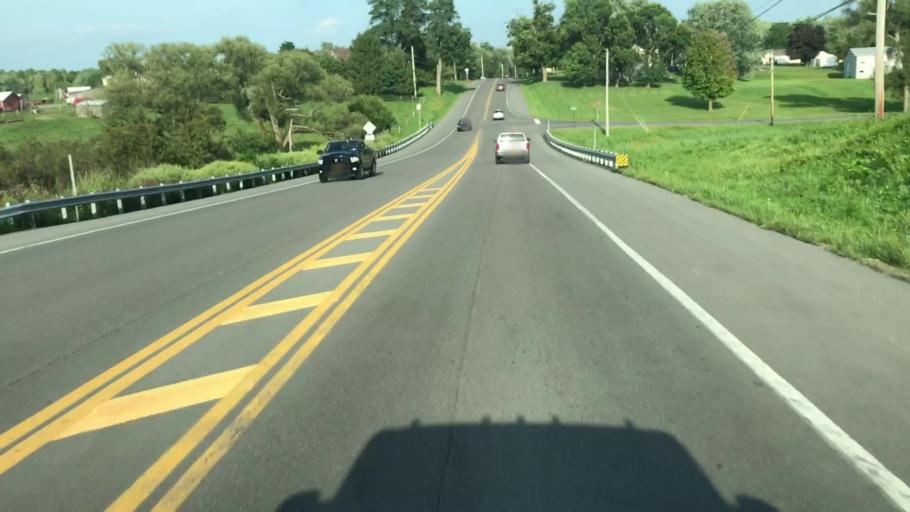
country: US
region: New York
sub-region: Onondaga County
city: Skaneateles
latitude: 42.9426
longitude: -76.4731
